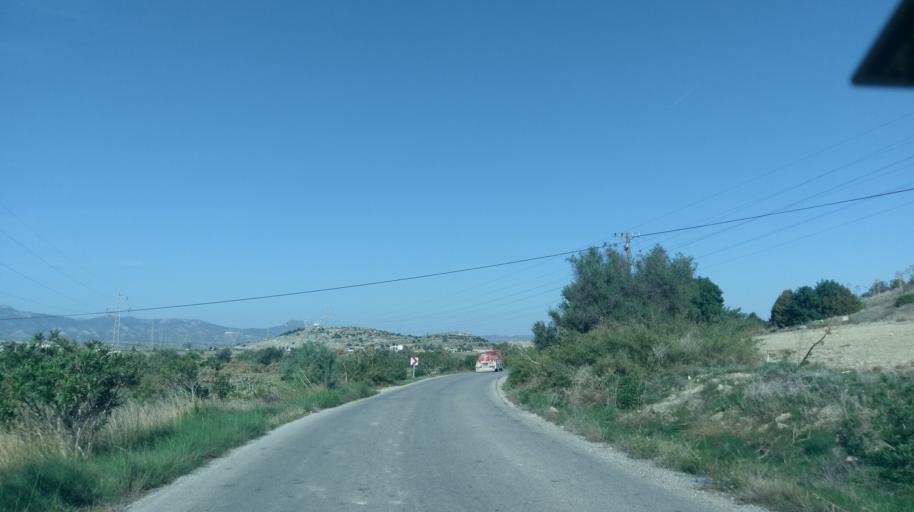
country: CY
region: Ammochostos
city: Trikomo
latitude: 35.3318
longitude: 33.9924
